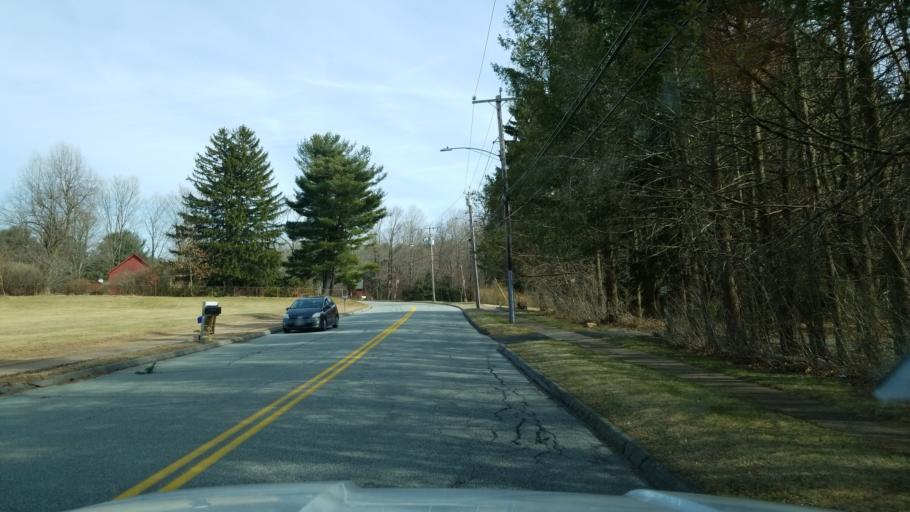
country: US
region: Connecticut
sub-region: Hartford County
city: Glastonbury Center
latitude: 41.7003
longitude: -72.5476
